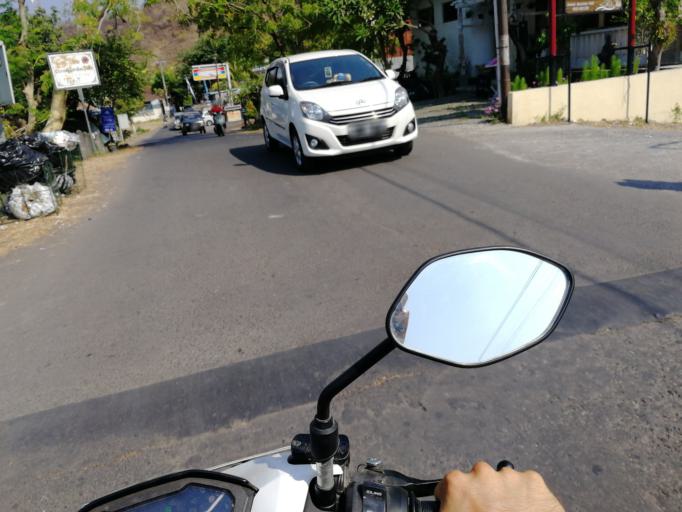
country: ID
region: Bali
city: Biaslantang Kaler
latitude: -8.3448
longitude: 115.6707
